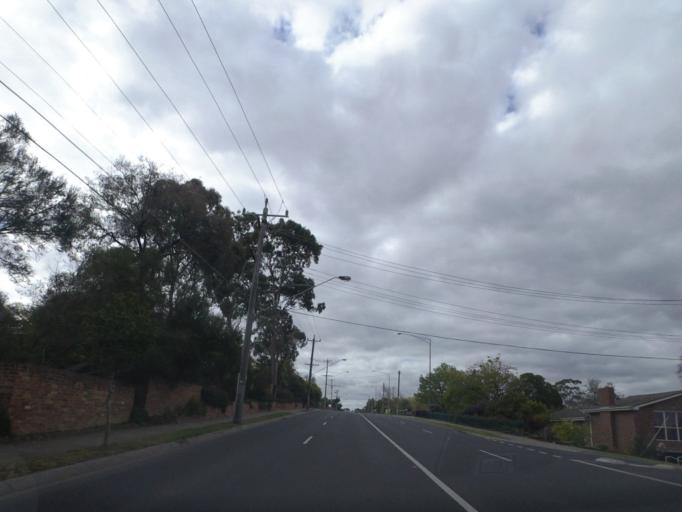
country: AU
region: Victoria
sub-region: Manningham
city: Templestowe Lower
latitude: -37.7781
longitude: 145.1134
